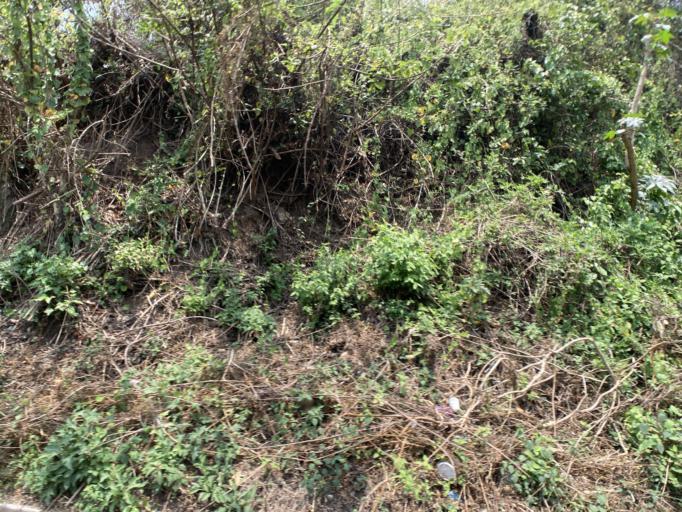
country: GT
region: Guatemala
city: Villa Canales
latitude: 14.3965
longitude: -90.5464
